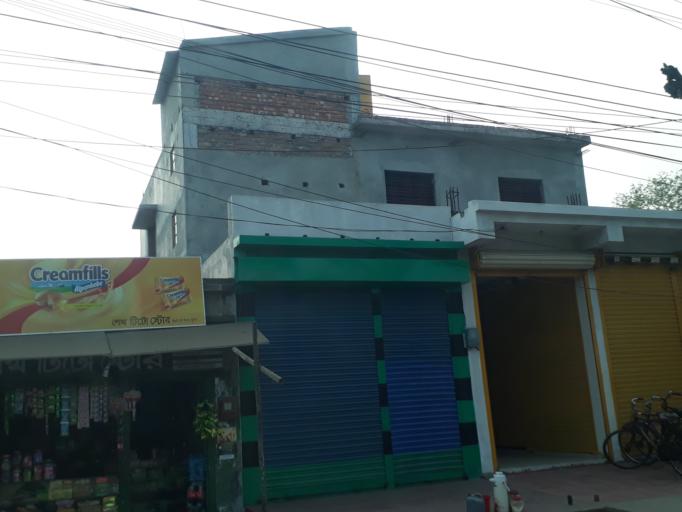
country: BD
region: Khulna
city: Bhatpara Abhaynagar
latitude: 22.9420
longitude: 89.4839
